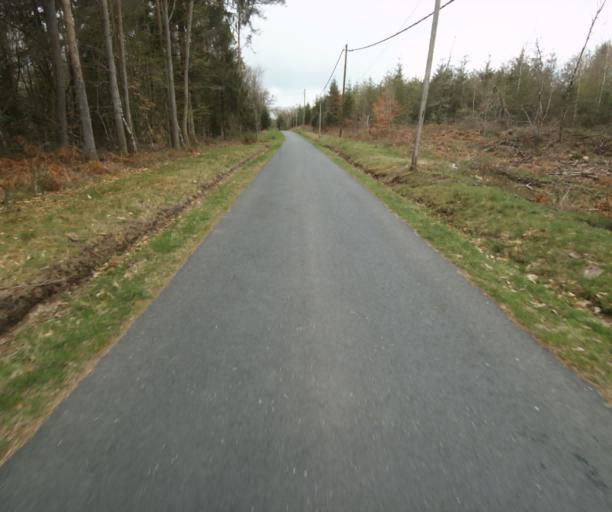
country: FR
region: Limousin
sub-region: Departement de la Correze
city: Correze
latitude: 45.3021
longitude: 1.9126
